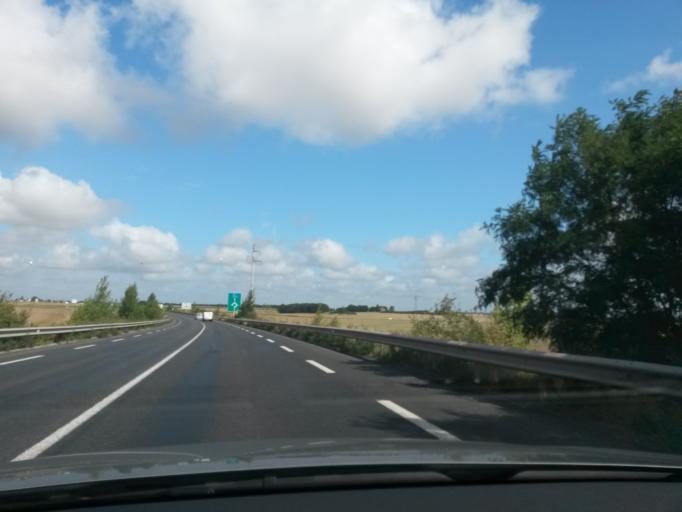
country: FR
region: Centre
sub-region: Departement d'Eure-et-Loir
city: Chateaudun
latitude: 48.0866
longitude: 1.3604
